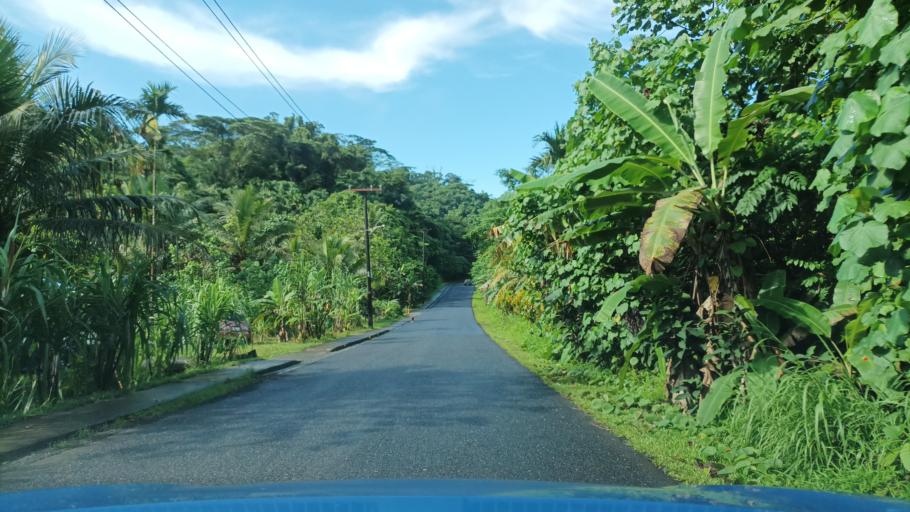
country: FM
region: Pohnpei
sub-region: Sokehs Municipality
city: Palikir - National Government Center
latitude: 6.9297
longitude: 158.1791
